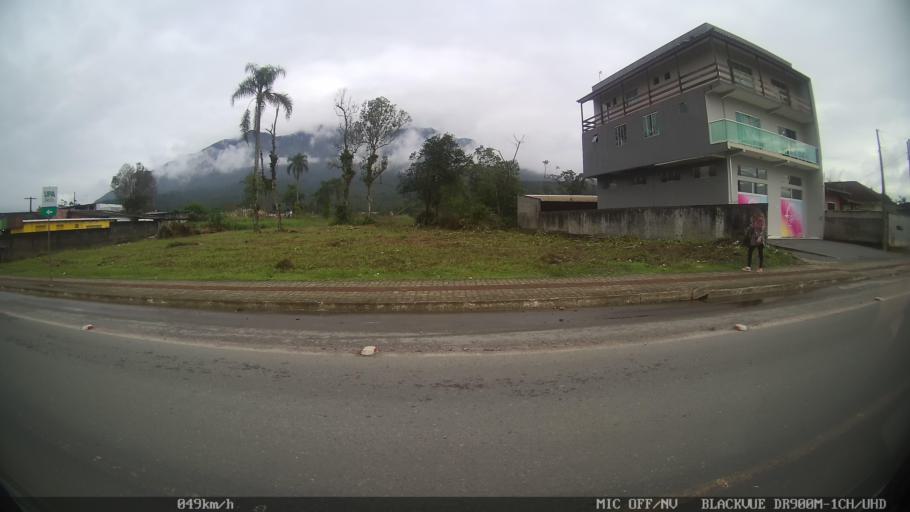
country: BR
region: Santa Catarina
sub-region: Joinville
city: Joinville
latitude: -26.0396
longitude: -48.8570
